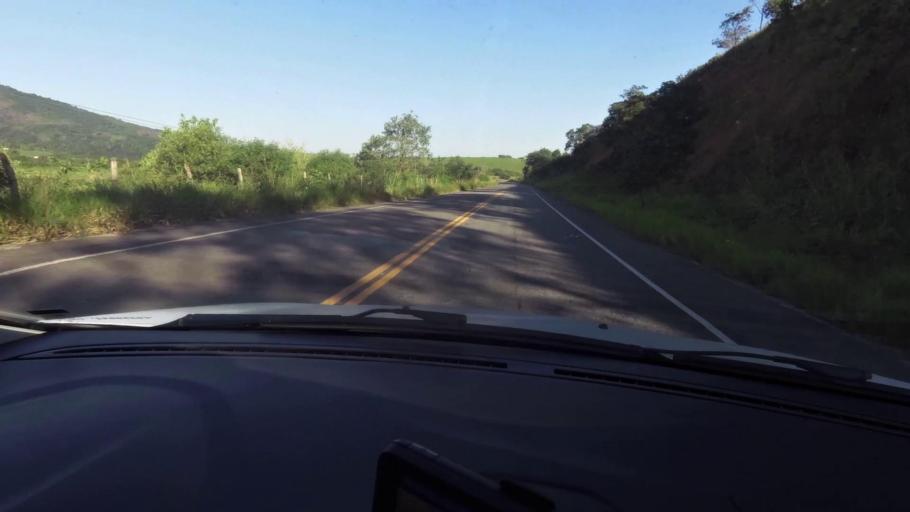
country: BR
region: Espirito Santo
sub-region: Piuma
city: Piuma
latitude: -20.7341
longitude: -40.6510
